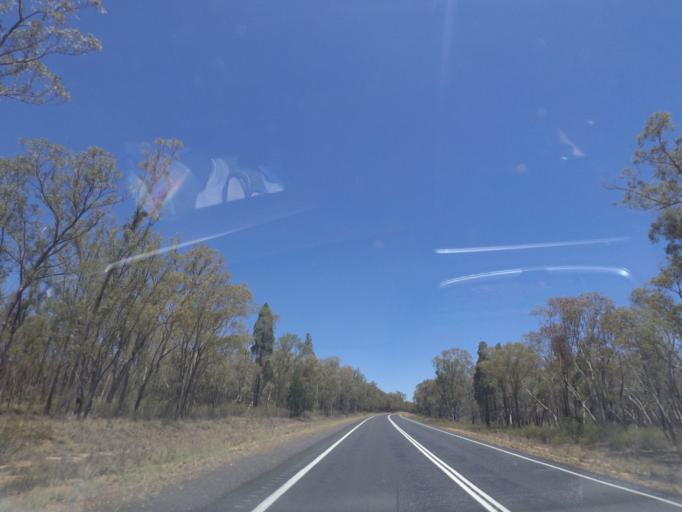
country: AU
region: New South Wales
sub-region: Warrumbungle Shire
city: Coonabarabran
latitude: -31.1904
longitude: 149.3539
